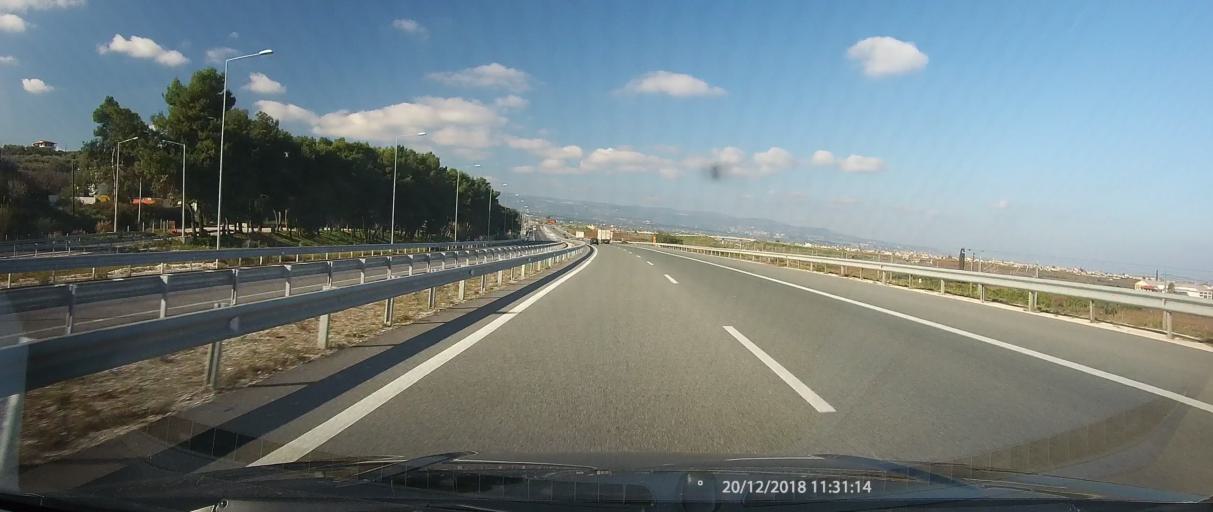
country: GR
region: Peloponnese
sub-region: Nomos Korinthias
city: Assos
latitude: 37.9205
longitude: 22.8175
